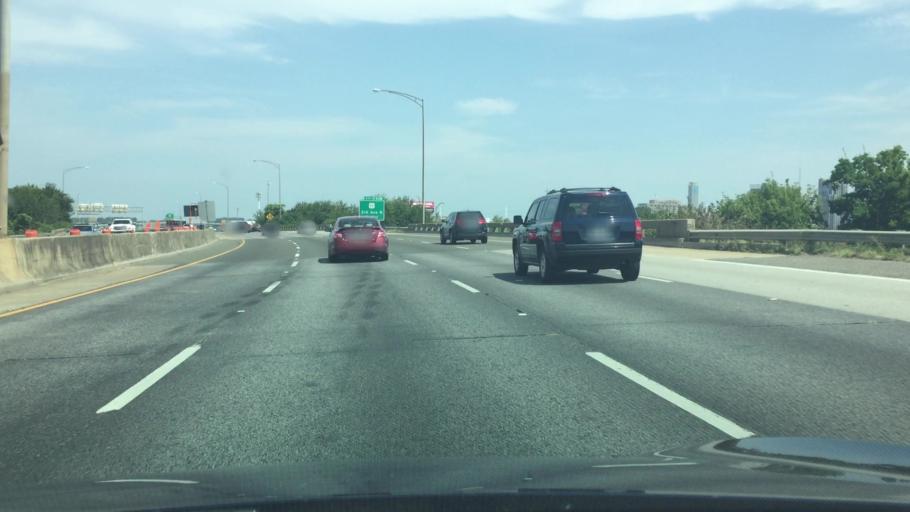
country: US
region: Alabama
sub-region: Jefferson County
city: Birmingham
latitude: 33.5014
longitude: -86.8144
